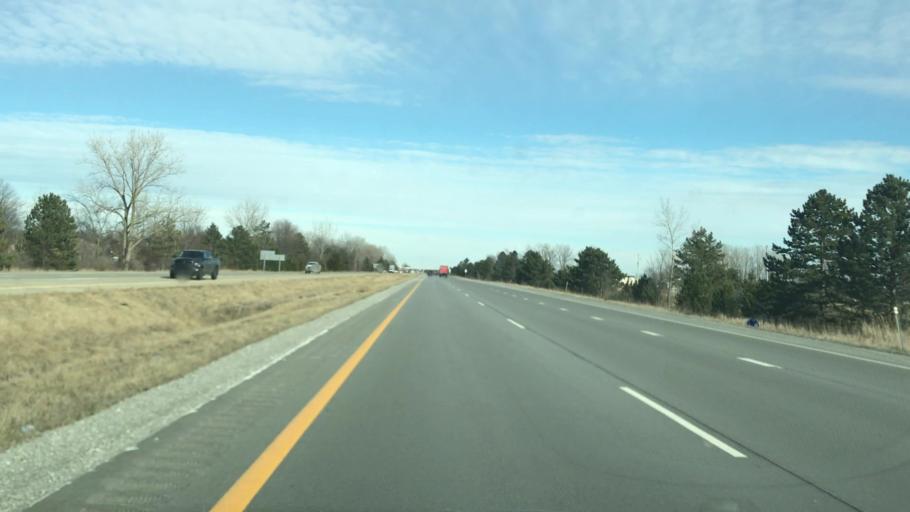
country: US
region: Michigan
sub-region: Bay County
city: Auburn
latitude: 43.5968
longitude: -84.0853
